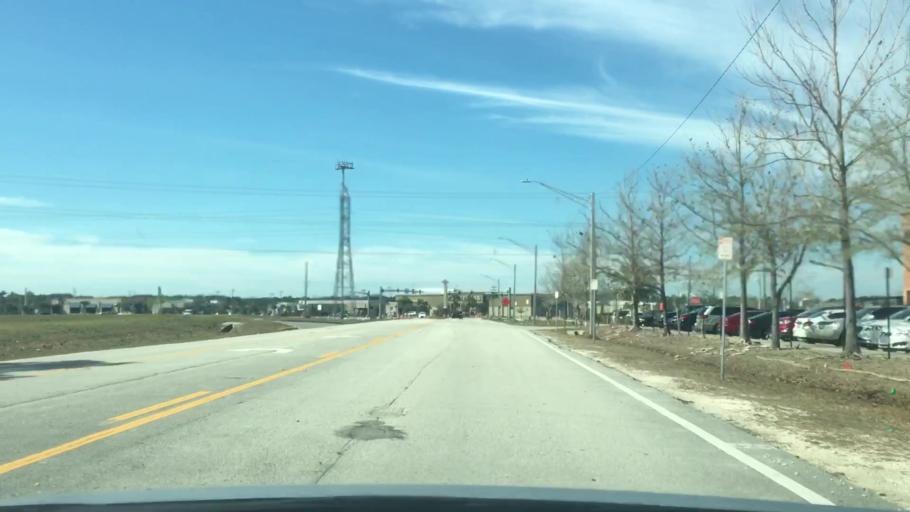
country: US
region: Florida
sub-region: Duval County
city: Atlantic Beach
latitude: 30.3223
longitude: -81.4872
